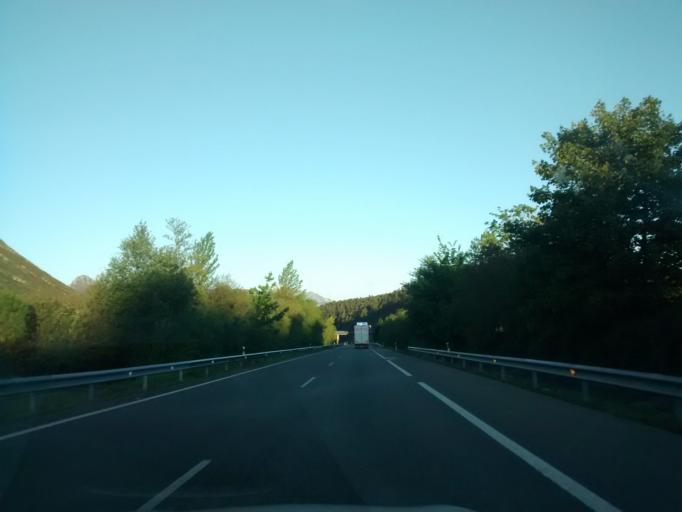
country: ES
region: Asturias
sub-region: Province of Asturias
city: Ribadesella
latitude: 43.4397
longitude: -5.0275
